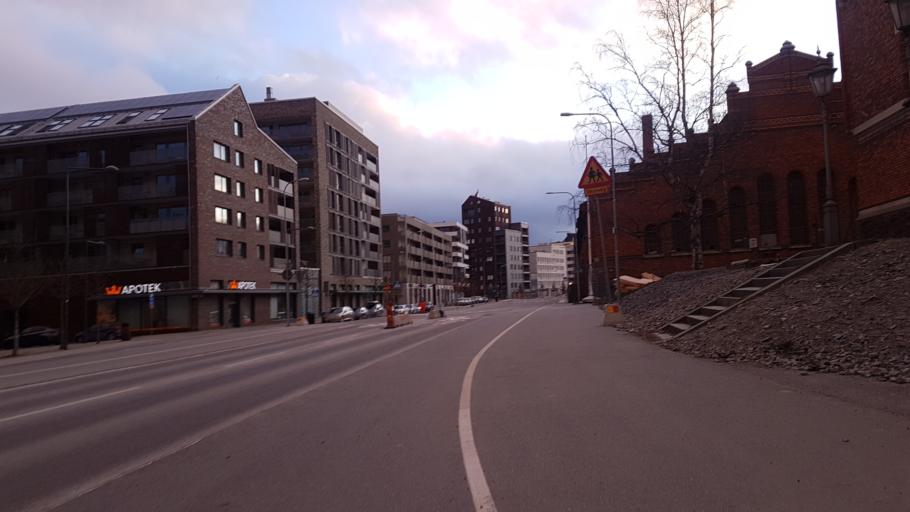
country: SE
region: Stockholm
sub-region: Stockholms Kommun
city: OEstermalm
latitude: 59.3579
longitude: 18.0900
